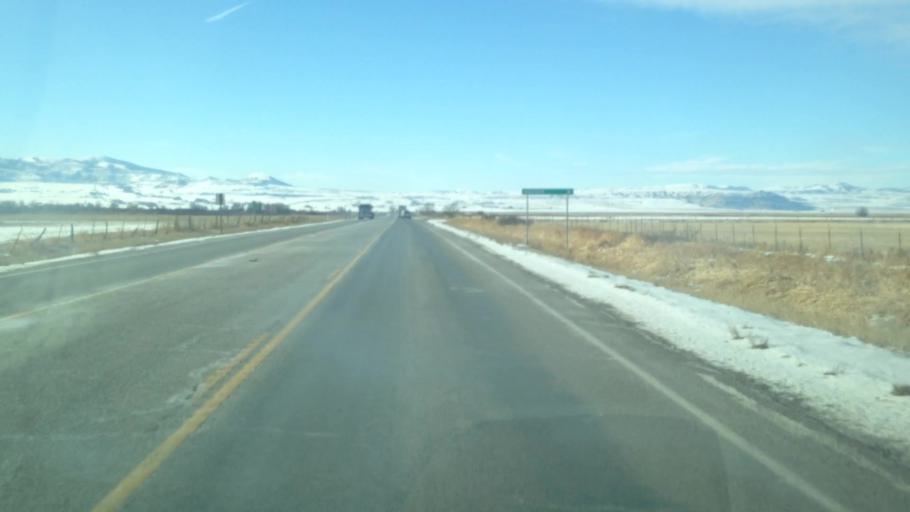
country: US
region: Utah
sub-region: Cache County
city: Benson
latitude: 41.7410
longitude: -111.9095
